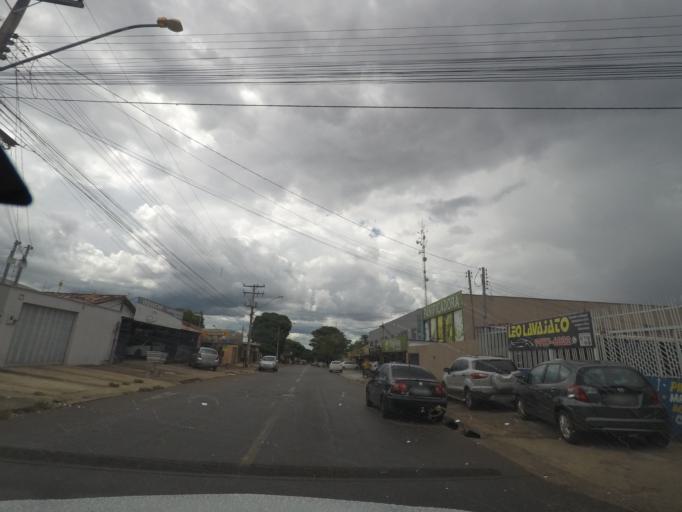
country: BR
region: Goias
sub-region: Goiania
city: Goiania
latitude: -16.7394
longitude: -49.3257
